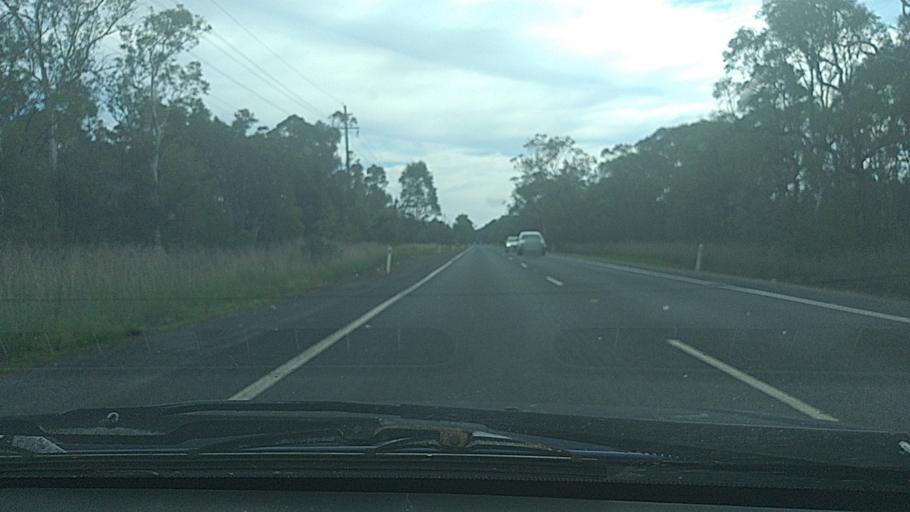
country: AU
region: New South Wales
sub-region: Penrith Municipality
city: Werrington Downs
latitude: -33.6757
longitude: 150.7470
